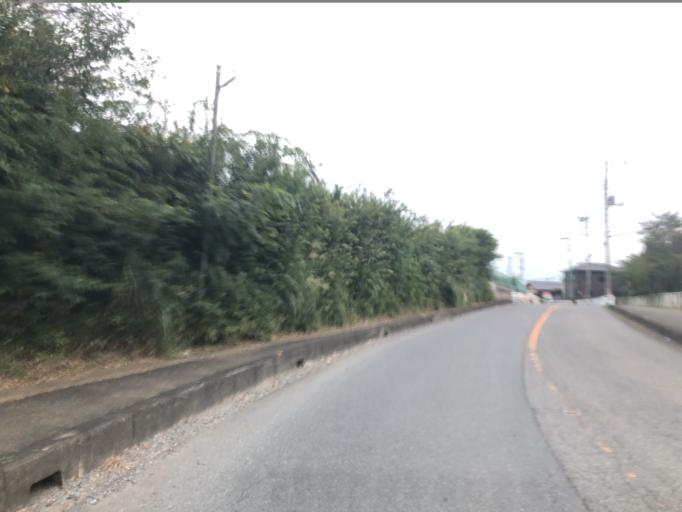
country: JP
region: Saitama
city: Fukiage-fujimi
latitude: 36.0509
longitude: 139.3902
